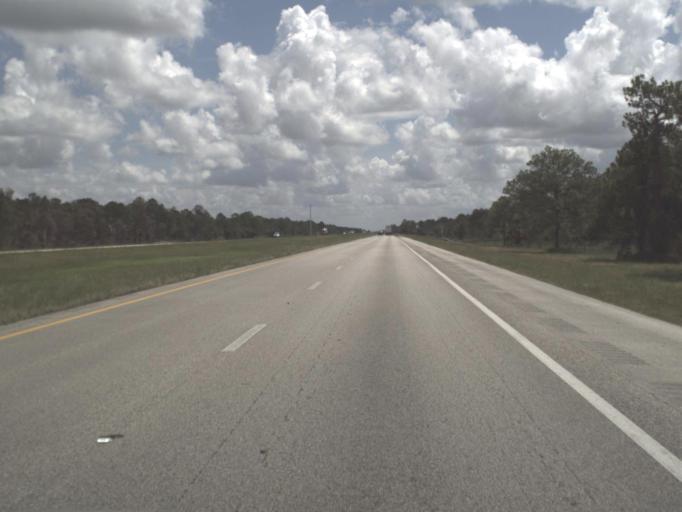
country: US
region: Florida
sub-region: Collier County
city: Golden Gate
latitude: 26.1535
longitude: -81.6003
